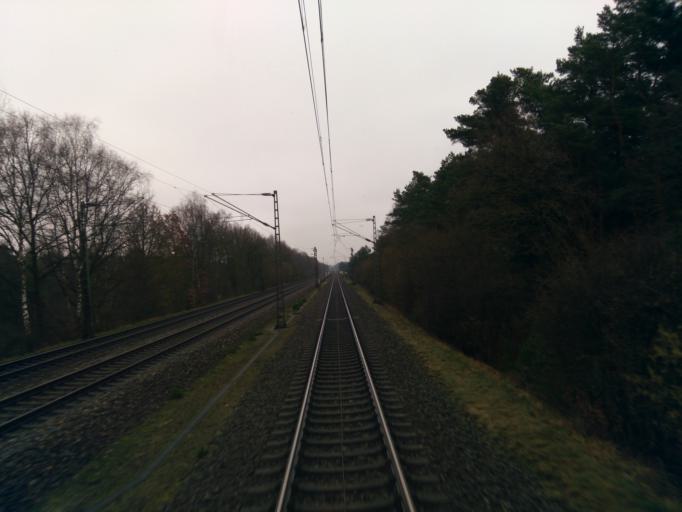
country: DE
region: Lower Saxony
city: Kakenstorf
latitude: 53.2870
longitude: 9.7647
